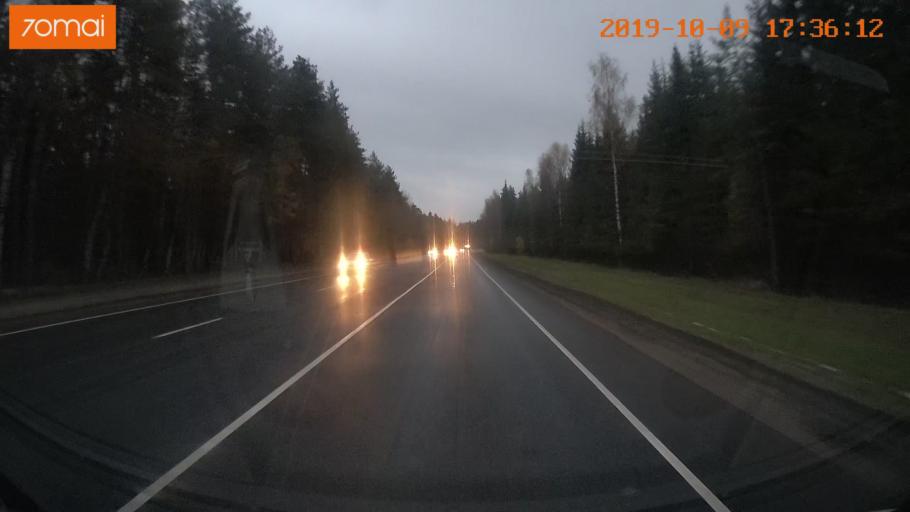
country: RU
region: Ivanovo
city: Bogorodskoye
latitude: 57.0820
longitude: 40.9981
